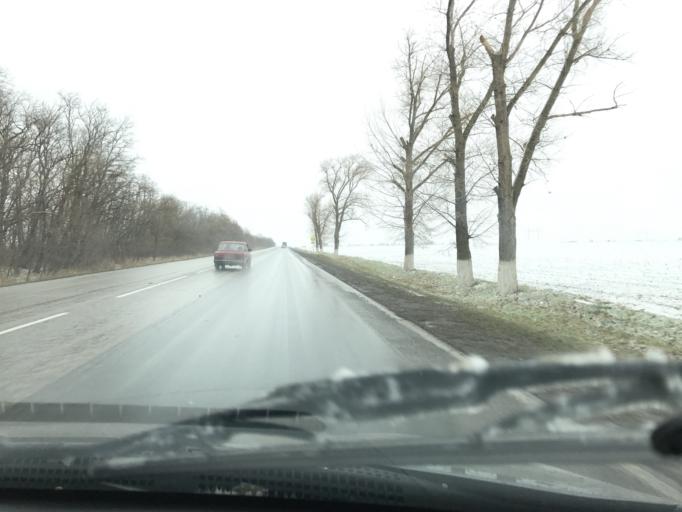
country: RU
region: Rostov
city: Zernograd
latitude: 46.8277
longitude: 40.2449
